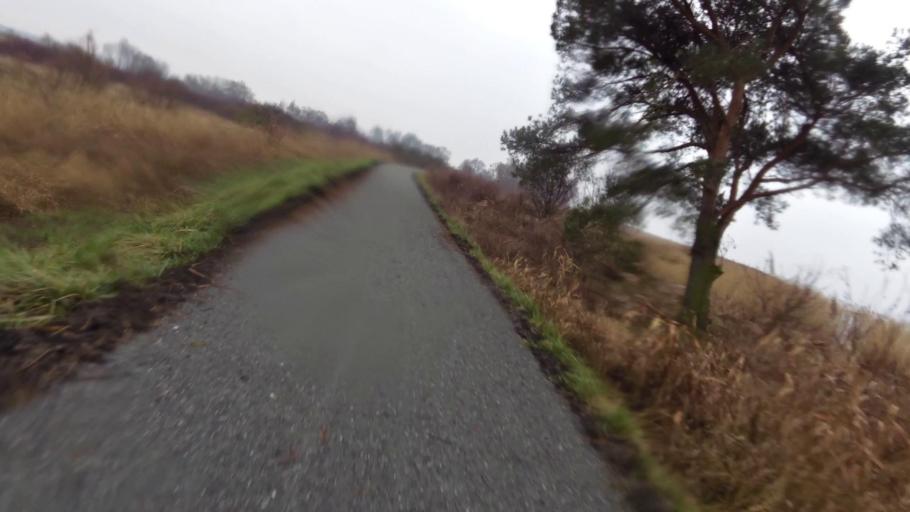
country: PL
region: West Pomeranian Voivodeship
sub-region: Powiat policki
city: Police
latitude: 53.4912
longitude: 14.6947
